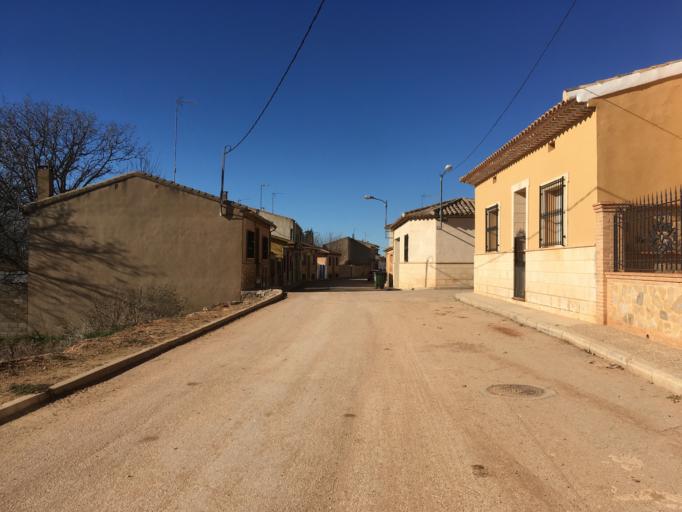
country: ES
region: Castille-La Mancha
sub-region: Provincia de Cuenca
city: Atalaya del Canavate
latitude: 39.5475
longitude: -2.2474
